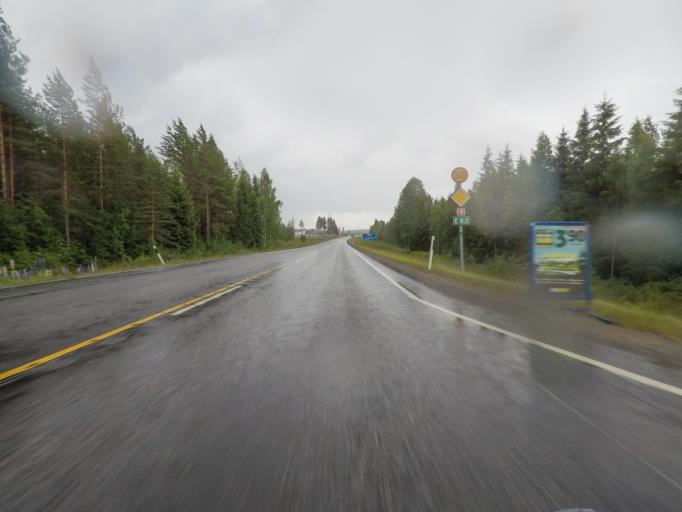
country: FI
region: Central Finland
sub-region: Jyvaeskylae
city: Hankasalmi
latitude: 62.3621
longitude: 26.5721
